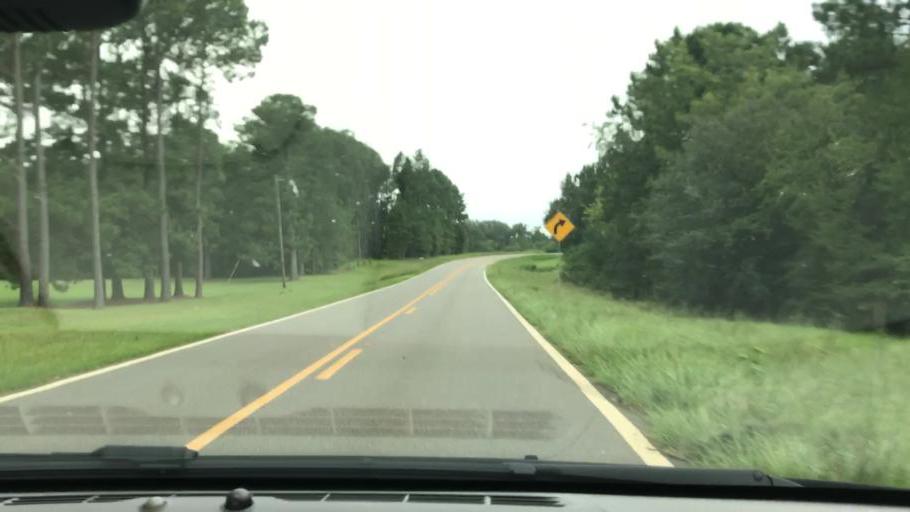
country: US
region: Georgia
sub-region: Early County
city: Blakely
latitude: 31.4453
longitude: -84.9133
